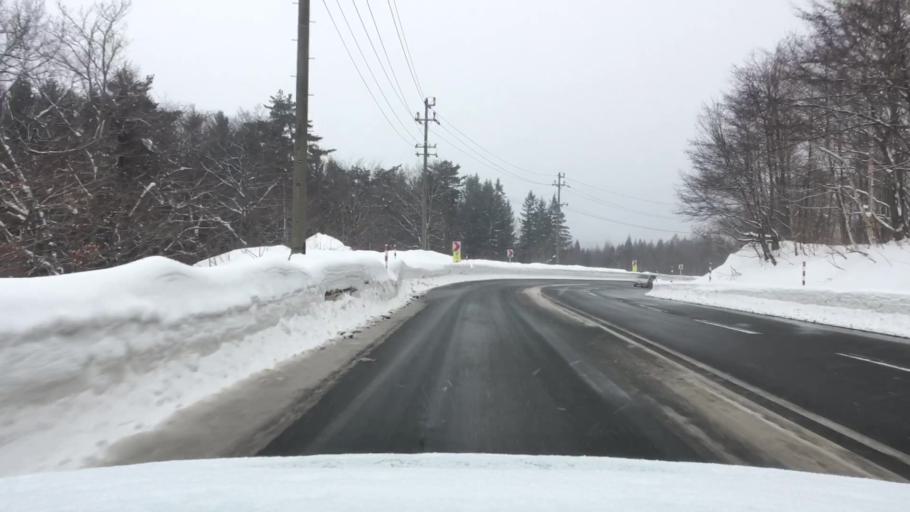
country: JP
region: Akita
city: Hanawa
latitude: 40.0222
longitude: 140.9869
